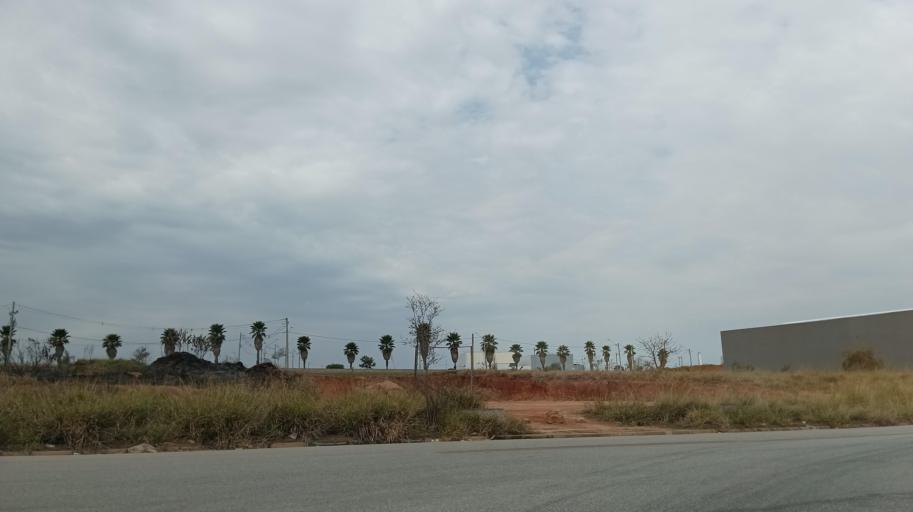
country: BR
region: Sao Paulo
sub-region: Sorocaba
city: Sorocaba
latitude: -23.4543
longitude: -47.4564
